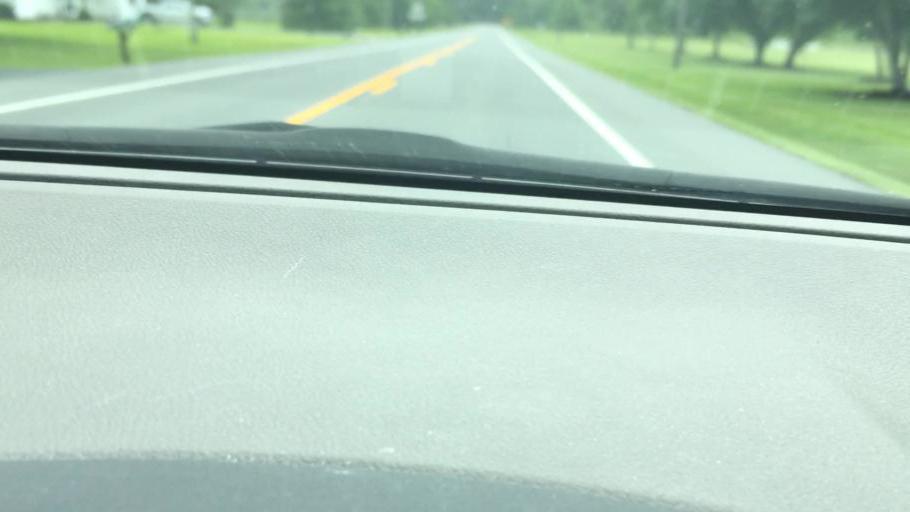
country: US
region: Maryland
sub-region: Worcester County
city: Pocomoke City
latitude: 38.0654
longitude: -75.5372
